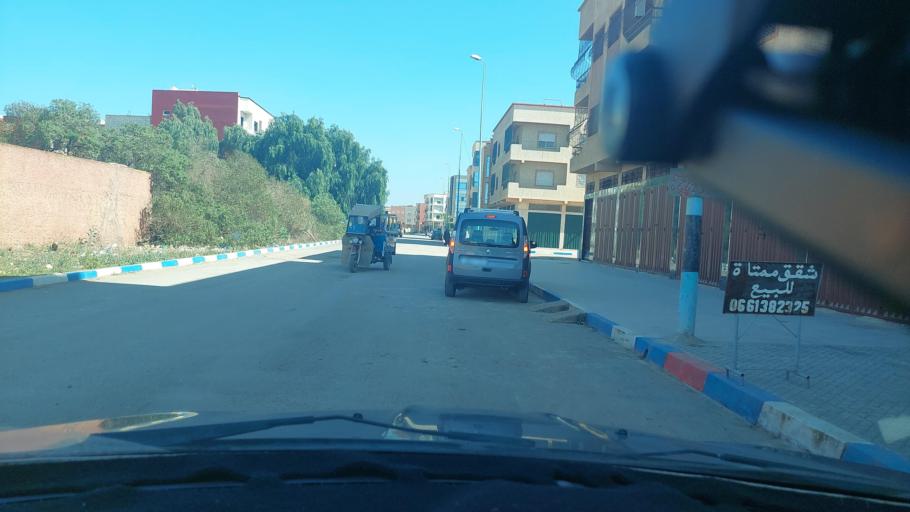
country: MA
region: Grand Casablanca
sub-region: Mediouna
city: Mediouna
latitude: 33.3787
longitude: -7.5374
